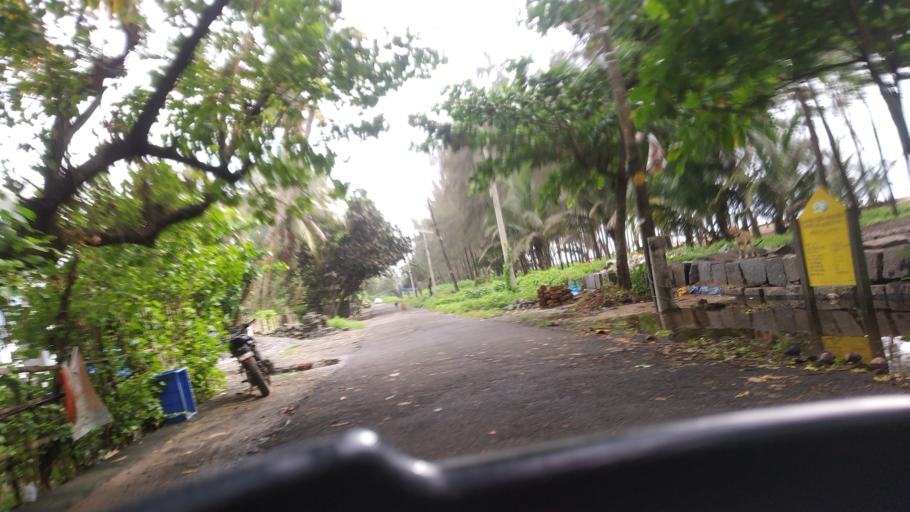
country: IN
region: Kerala
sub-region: Thrissur District
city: Kodungallur
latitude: 10.1254
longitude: 76.1837
